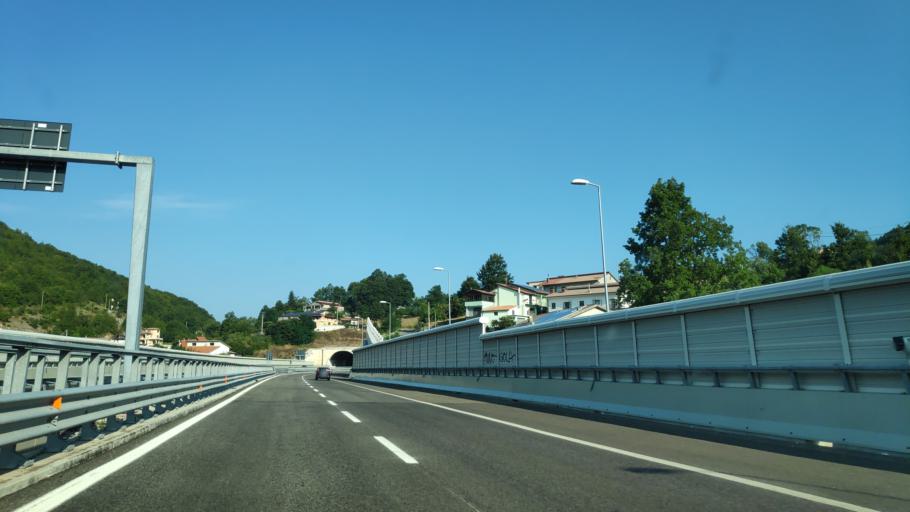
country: IT
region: Basilicate
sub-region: Provincia di Potenza
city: Lauria
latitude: 40.0201
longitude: 15.8831
